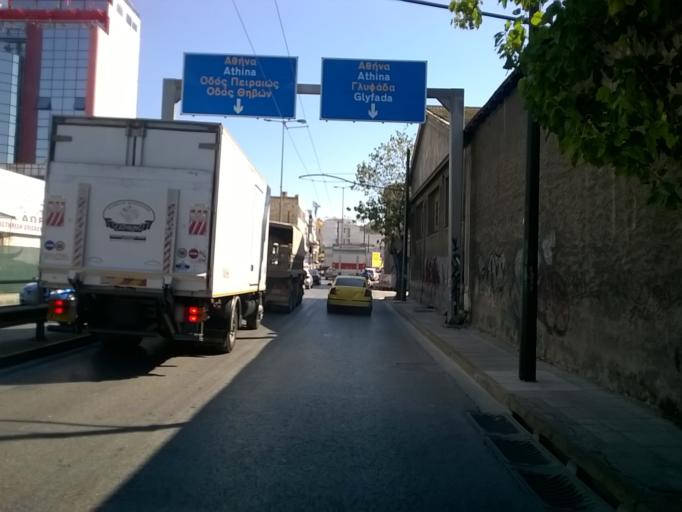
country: GR
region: Attica
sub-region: Nomos Attikis
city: Piraeus
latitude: 37.9489
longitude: 23.6456
